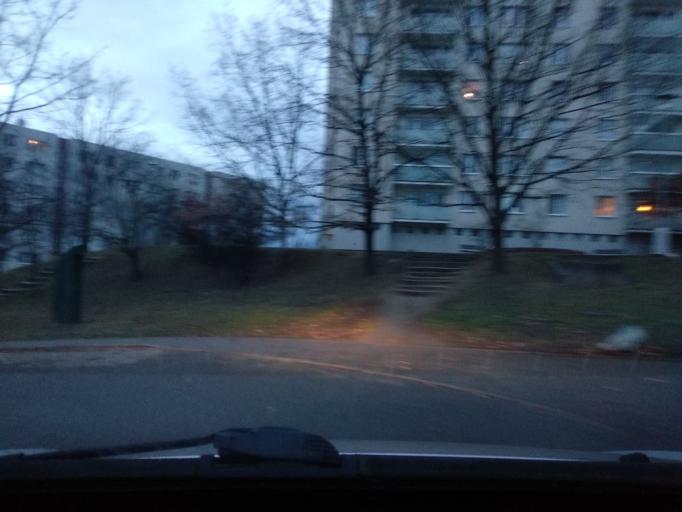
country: CZ
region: South Moravian
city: Ostopovice
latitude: 49.1761
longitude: 16.5527
